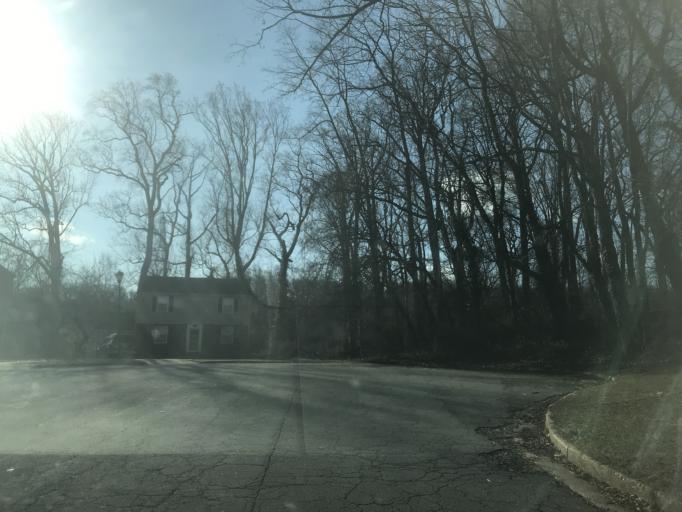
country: US
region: Maryland
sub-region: Baltimore County
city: Hampton
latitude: 39.4032
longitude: -76.5787
